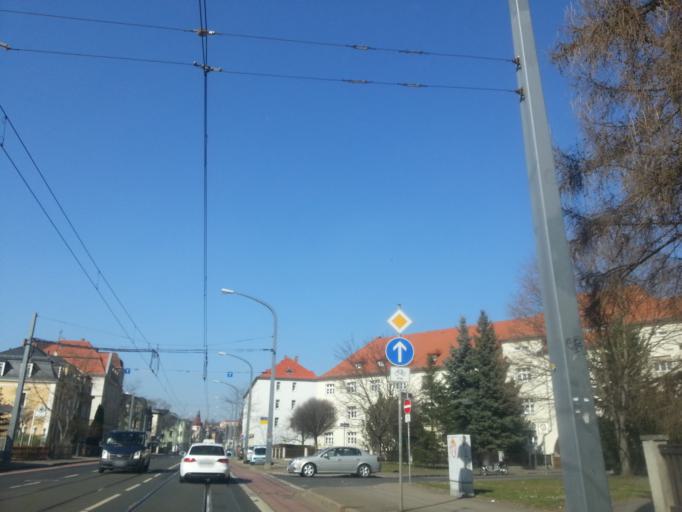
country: DE
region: Saxony
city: Dresden
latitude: 51.0911
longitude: 13.7223
